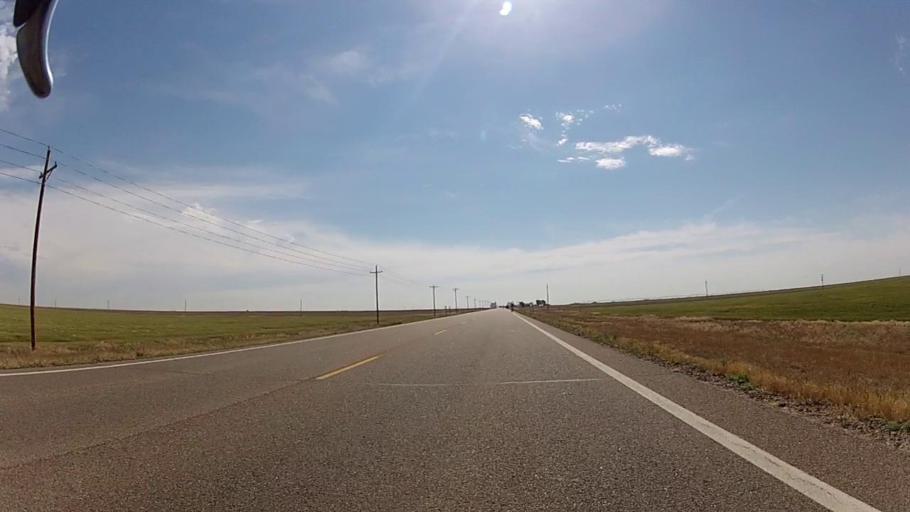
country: US
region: Kansas
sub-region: Grant County
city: Ulysses
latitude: 37.5618
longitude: -101.2721
